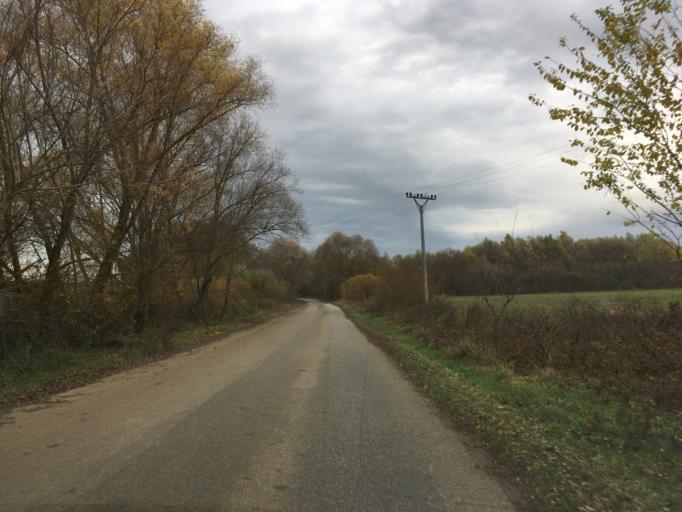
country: SK
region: Nitriansky
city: Svodin
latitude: 48.0391
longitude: 18.3726
